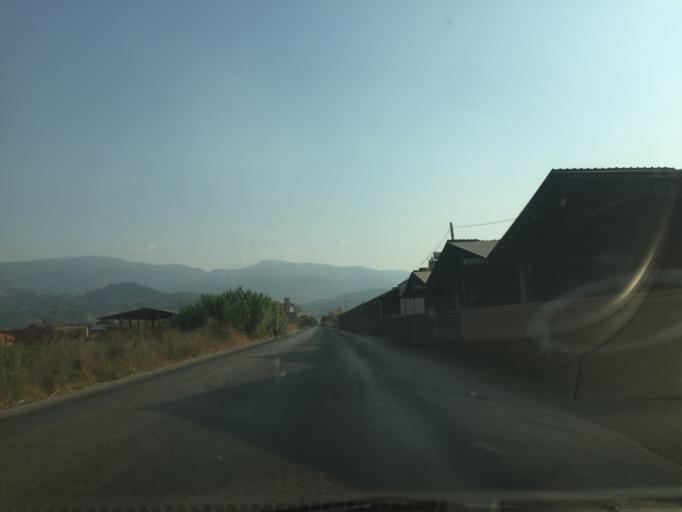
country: TR
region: Manisa
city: Salihli
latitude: 38.4998
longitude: 28.1843
